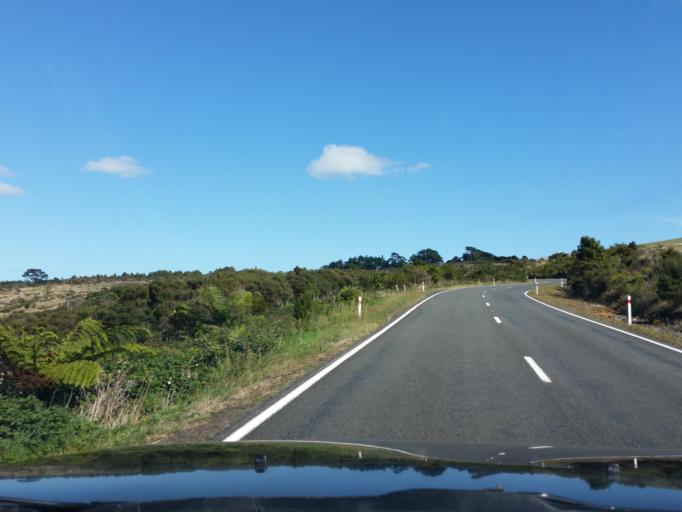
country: NZ
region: Northland
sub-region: Kaipara District
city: Dargaville
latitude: -35.6871
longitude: 173.5749
